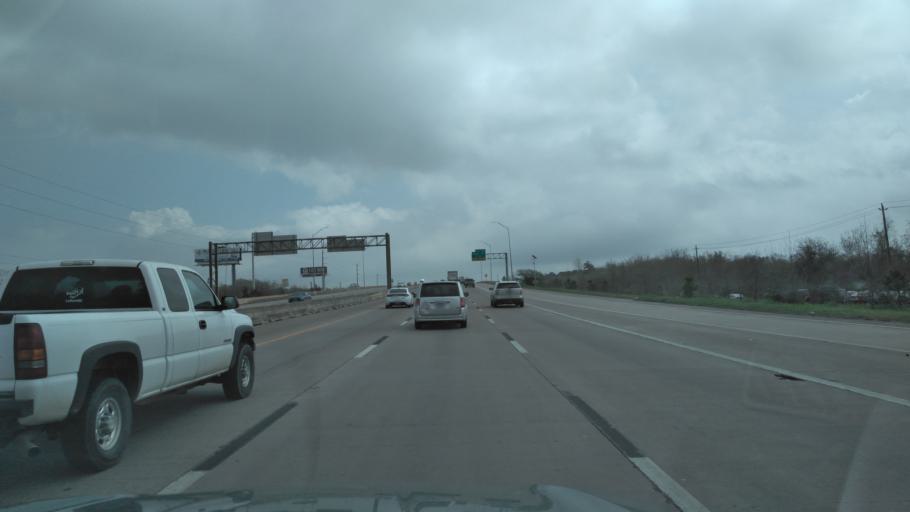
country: US
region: Texas
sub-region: Harris County
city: Highlands
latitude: 29.7999
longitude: -95.0214
